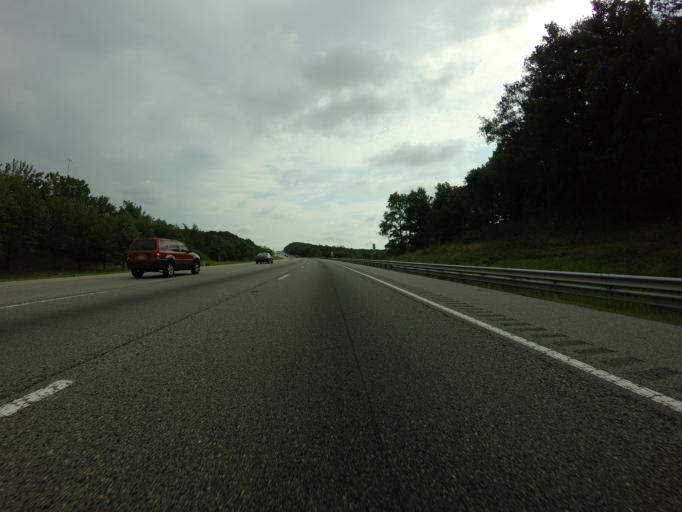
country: US
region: Maryland
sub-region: Cecil County
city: Charlestown
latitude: 39.6108
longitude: -76.0066
